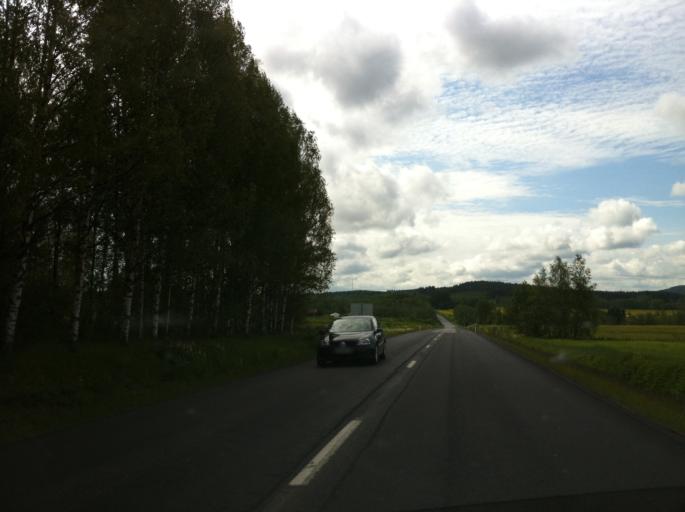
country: SE
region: Vaermland
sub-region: Sunne Kommun
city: Sunne
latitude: 59.7320
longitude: 13.1326
